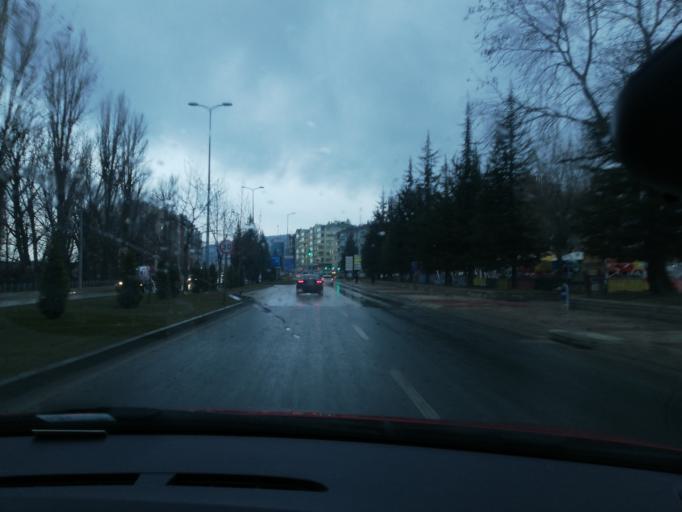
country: TR
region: Kastamonu
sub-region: Cide
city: Kastamonu
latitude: 41.4080
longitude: 33.7877
